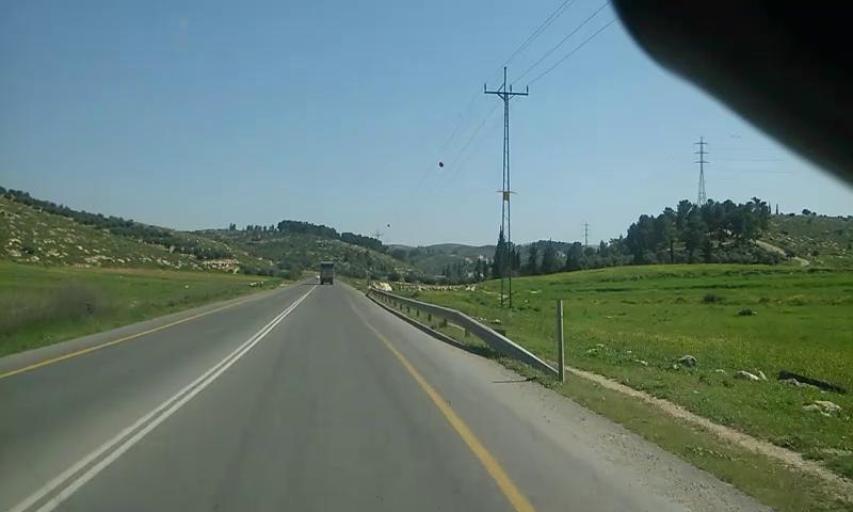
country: PS
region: West Bank
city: Idhna
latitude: 31.5765
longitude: 34.9803
